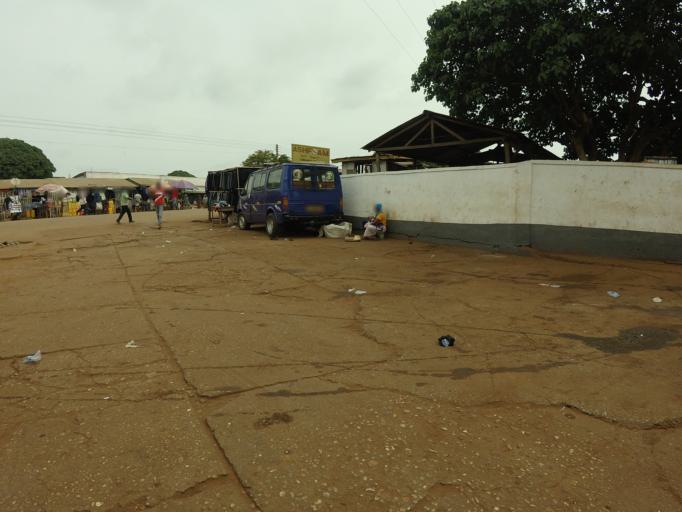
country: GH
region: Northern
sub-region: Yendi
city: Yendi
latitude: 9.4405
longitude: -0.0067
